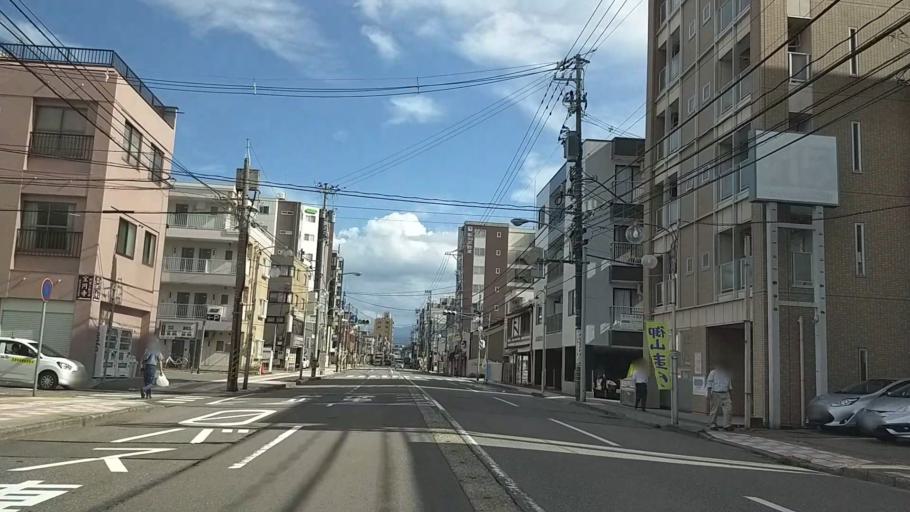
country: JP
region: Ishikawa
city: Nonoichi
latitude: 36.5563
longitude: 136.6695
